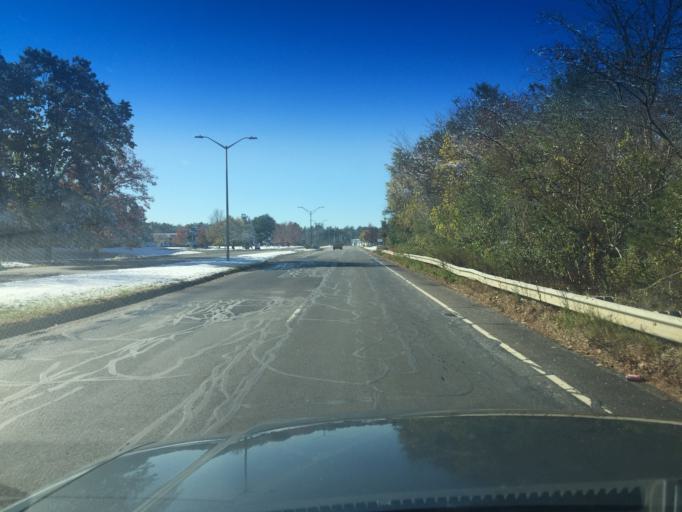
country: US
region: Massachusetts
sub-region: Bristol County
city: Norton
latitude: 41.9499
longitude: -71.1398
